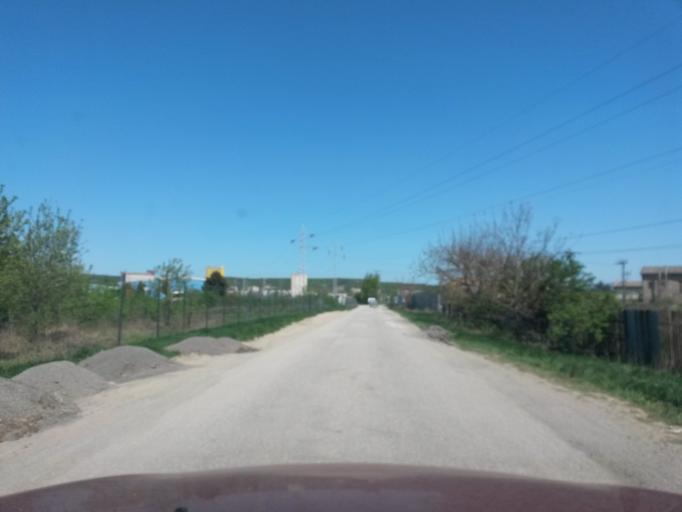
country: SK
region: Kosicky
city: Kosice
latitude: 48.6722
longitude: 21.2727
